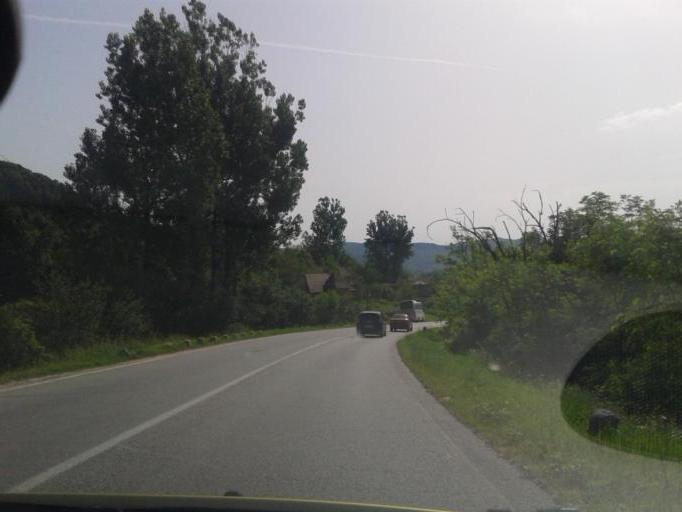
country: RO
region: Valcea
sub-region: Comuna Pietrari
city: Pietrari
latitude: 45.1089
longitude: 24.1415
